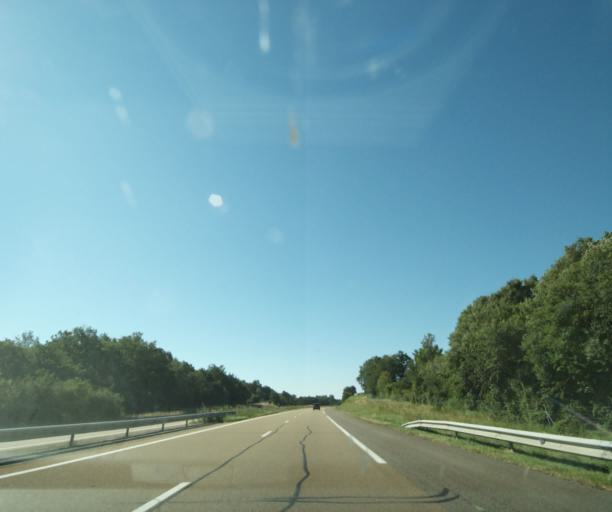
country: FR
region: Champagne-Ardenne
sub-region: Departement de la Haute-Marne
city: Rolampont
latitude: 47.9231
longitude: 5.2181
